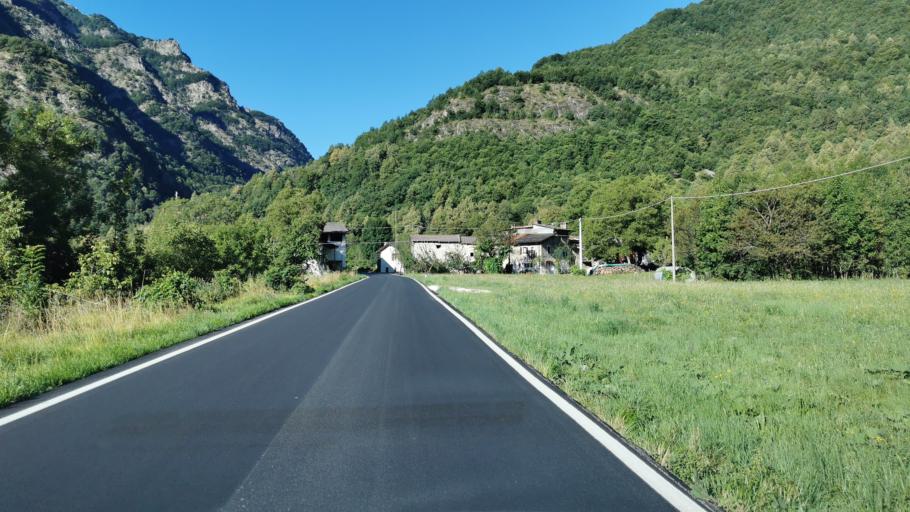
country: IT
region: Piedmont
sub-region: Provincia di Cuneo
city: Valdieri
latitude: 44.2582
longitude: 7.3555
